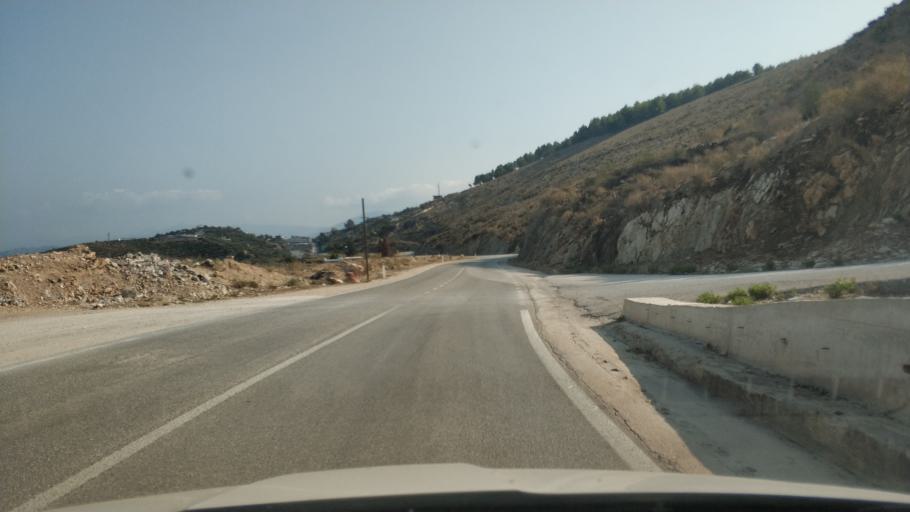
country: AL
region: Vlore
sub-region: Rrethi i Sarandes
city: Sarande
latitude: 39.8879
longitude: 20.0176
